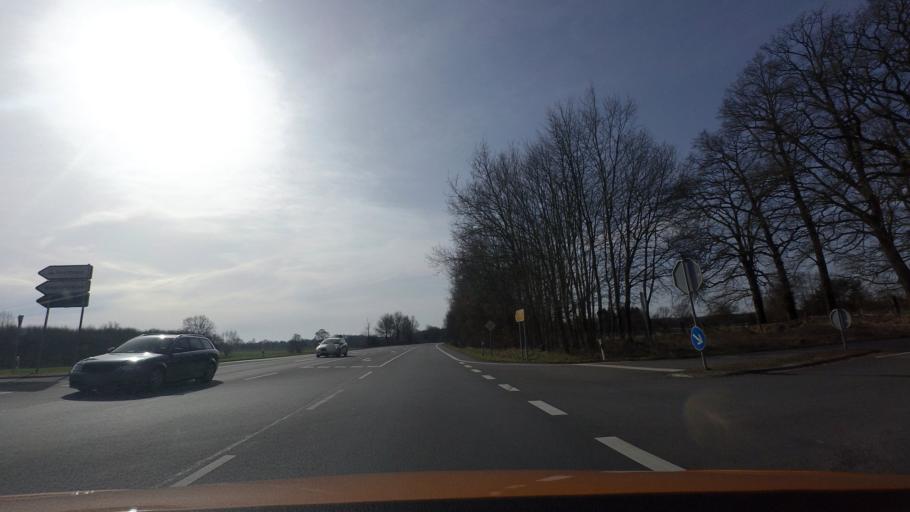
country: DE
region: North Rhine-Westphalia
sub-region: Regierungsbezirk Detmold
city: Petershagen
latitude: 52.3905
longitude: 8.9571
